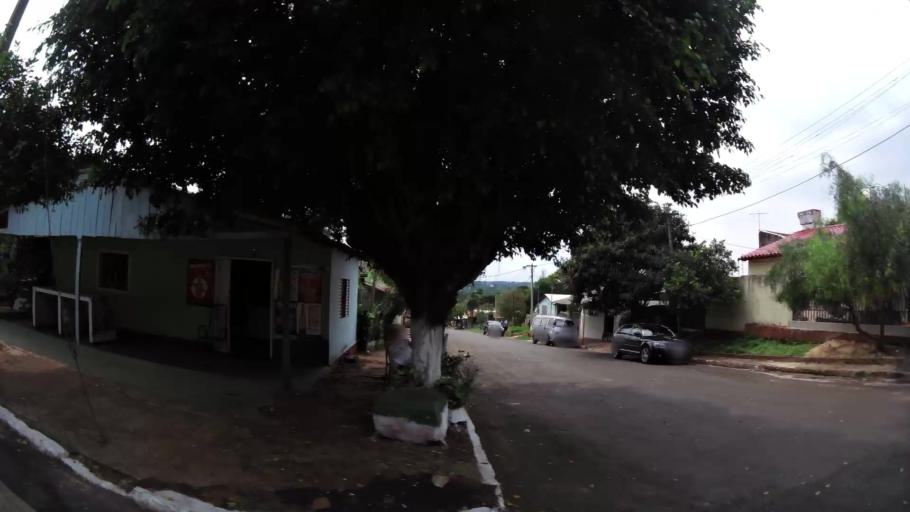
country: BR
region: Parana
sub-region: Foz Do Iguacu
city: Foz do Iguacu
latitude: -25.5548
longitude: -54.6059
